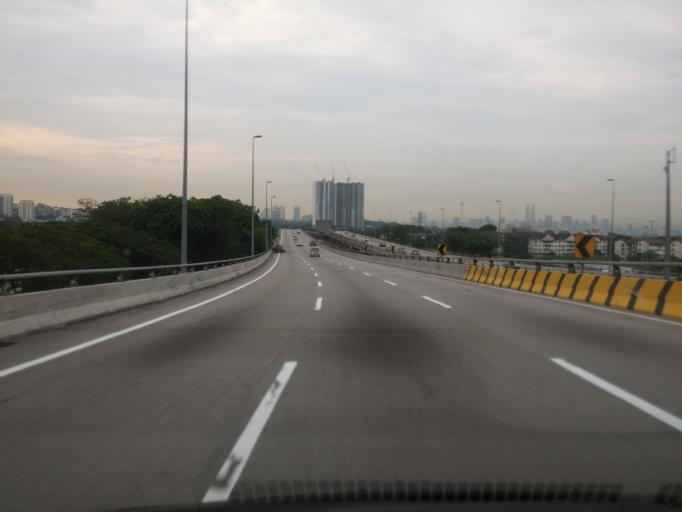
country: MY
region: Kuala Lumpur
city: Kuala Lumpur
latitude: 3.0910
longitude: 101.6964
